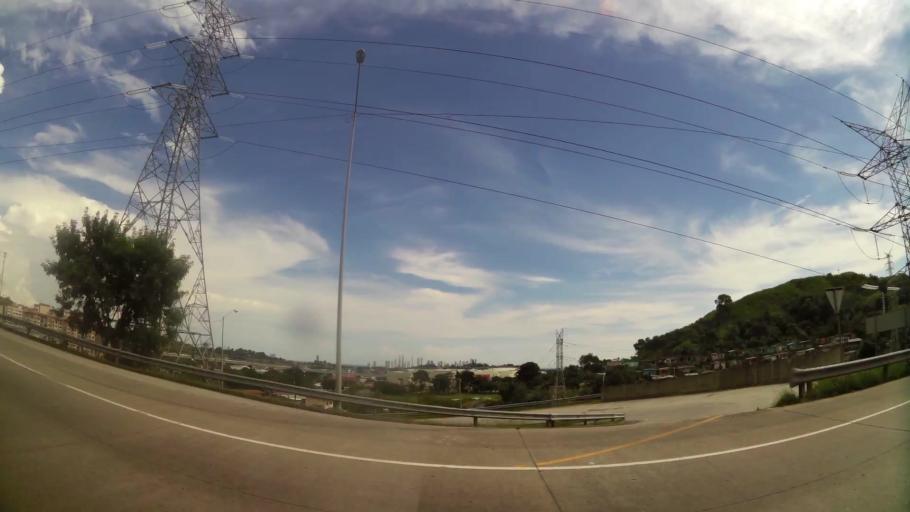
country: PA
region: Panama
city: Las Cumbres
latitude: 9.0575
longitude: -79.5121
